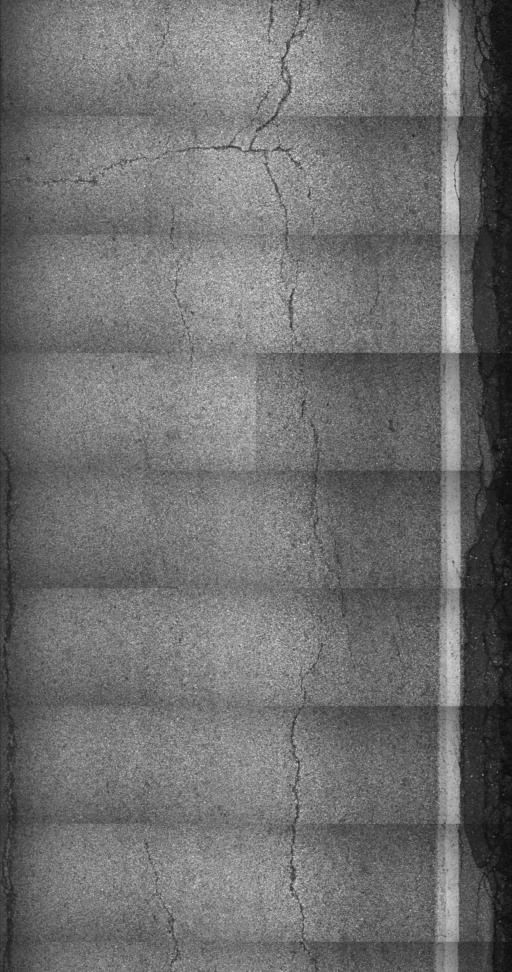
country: US
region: Vermont
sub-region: Rutland County
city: Rutland
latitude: 43.6958
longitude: -73.0111
